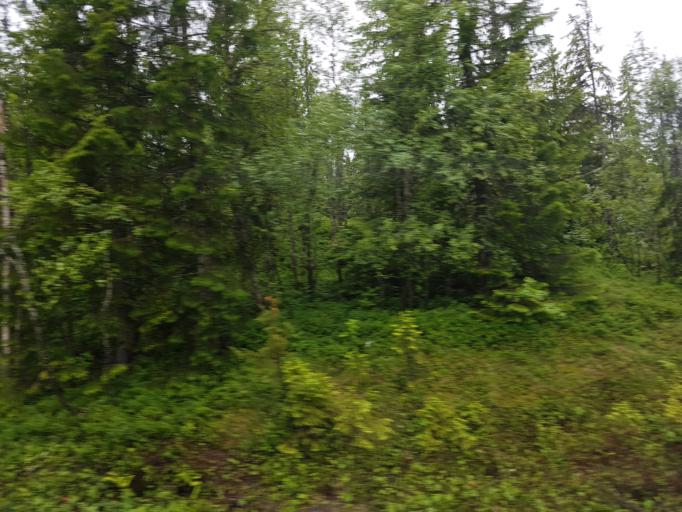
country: NO
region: Sor-Trondelag
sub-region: Selbu
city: Mebonden
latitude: 63.3391
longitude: 11.0811
